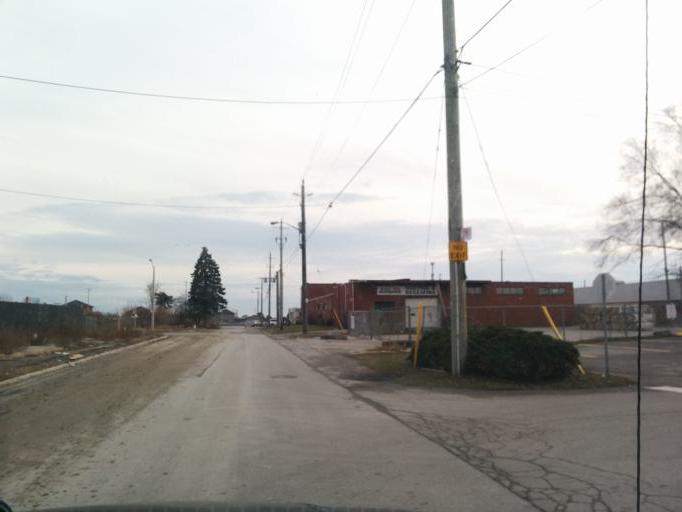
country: CA
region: Ontario
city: Etobicoke
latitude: 43.6209
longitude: -79.5219
